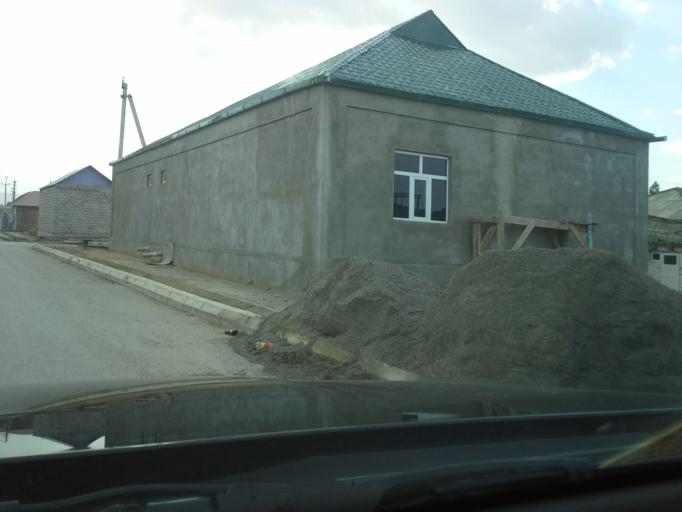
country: TM
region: Ahal
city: Ashgabat
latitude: 37.9945
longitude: 58.2971
